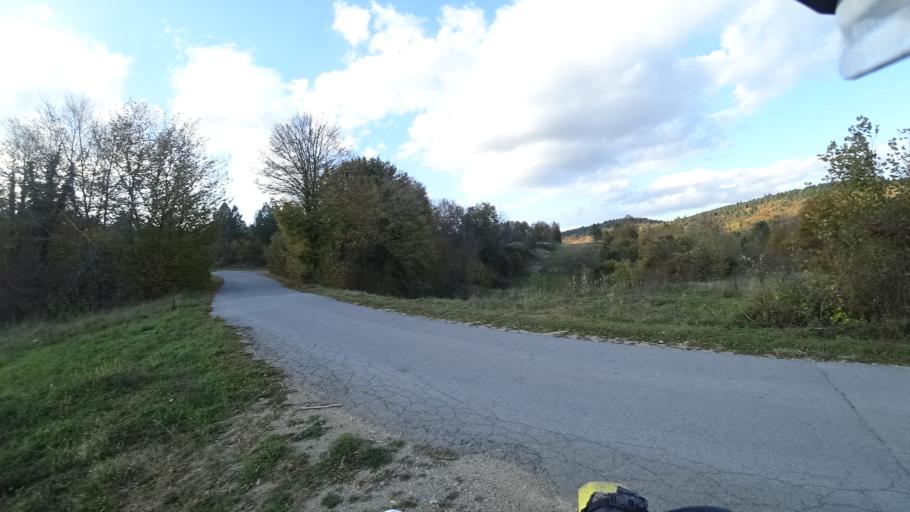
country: HR
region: Karlovacka
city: Plaski
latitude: 45.0029
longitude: 15.4257
